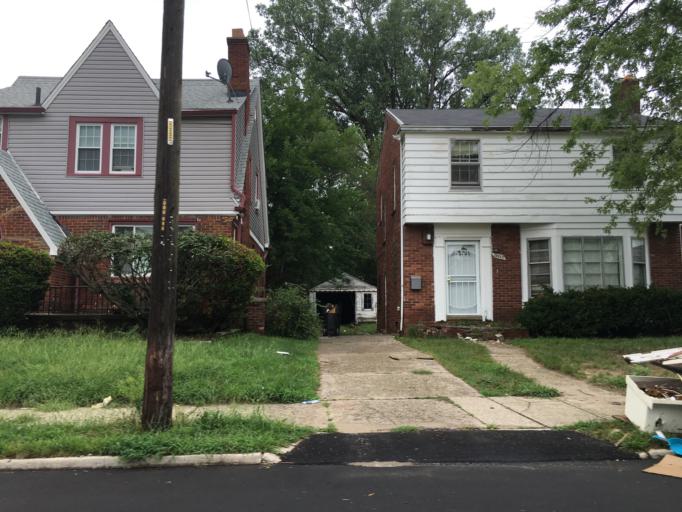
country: US
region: Michigan
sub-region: Oakland County
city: Ferndale
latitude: 42.4087
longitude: -83.1567
